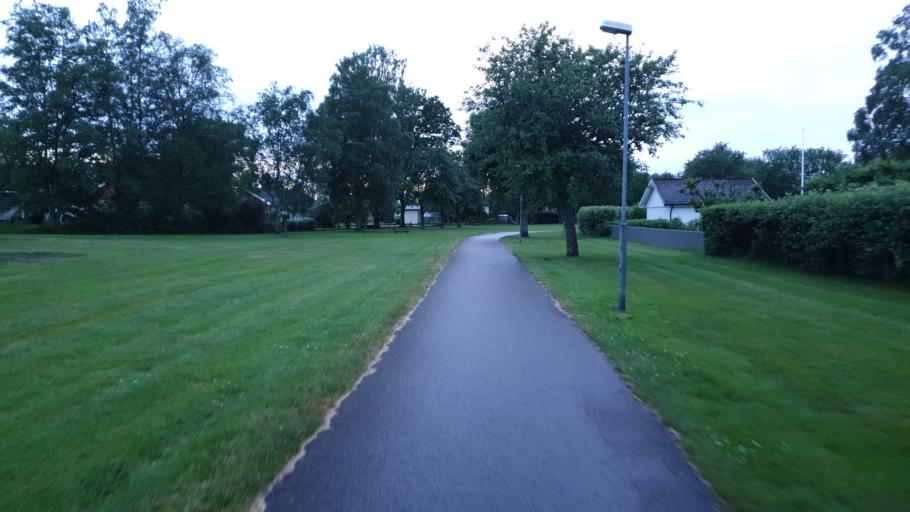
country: SE
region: Kronoberg
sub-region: Ljungby Kommun
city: Ljungby
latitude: 56.8269
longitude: 13.9518
